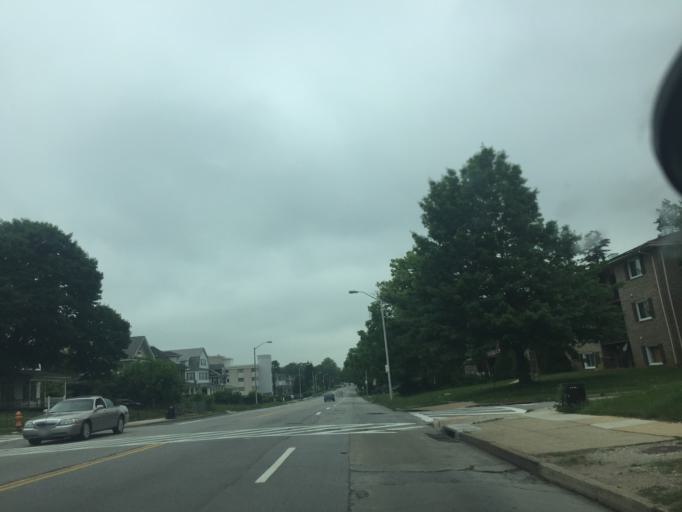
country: US
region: Maryland
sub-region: Baltimore County
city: Lochearn
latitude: 39.3281
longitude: -76.6849
